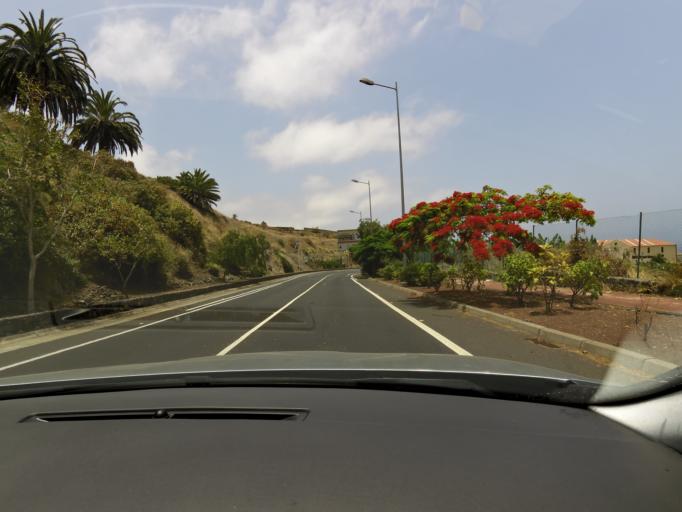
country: ES
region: Canary Islands
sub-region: Provincia de Santa Cruz de Tenerife
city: La Orotava
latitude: 28.4071
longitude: -16.5305
